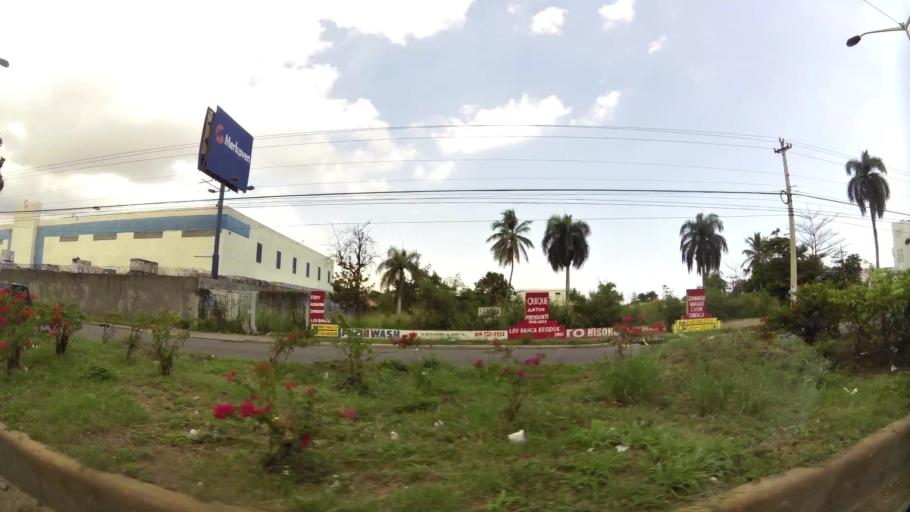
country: DO
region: Santo Domingo
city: Santo Domingo Oeste
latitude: 18.4964
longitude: -69.9992
